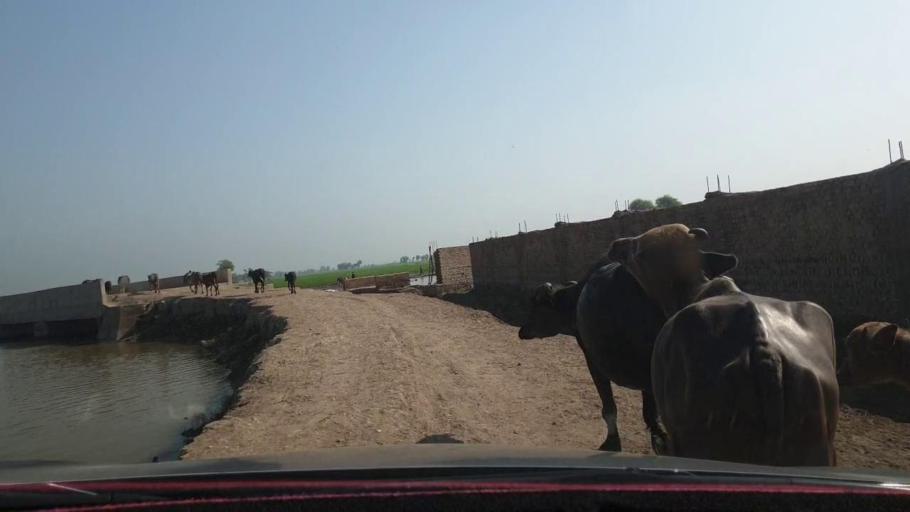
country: PK
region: Sindh
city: Nasirabad
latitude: 27.4644
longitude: 67.9201
